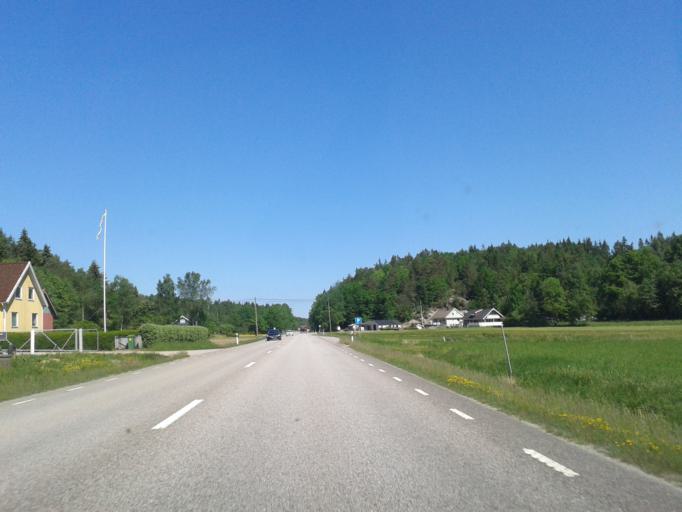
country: SE
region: Vaestra Goetaland
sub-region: Orust
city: Henan
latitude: 58.1809
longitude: 11.6953
